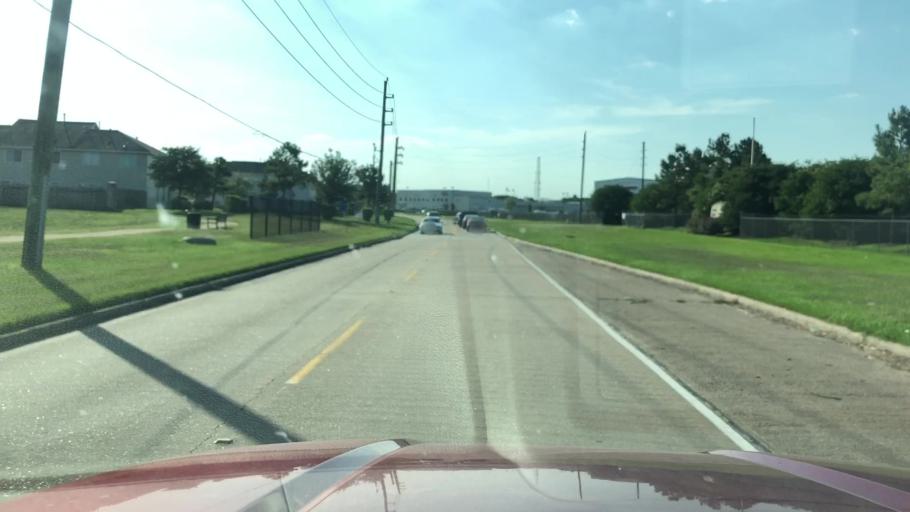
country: US
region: Texas
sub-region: Harris County
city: Hudson
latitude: 29.9448
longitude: -95.4934
